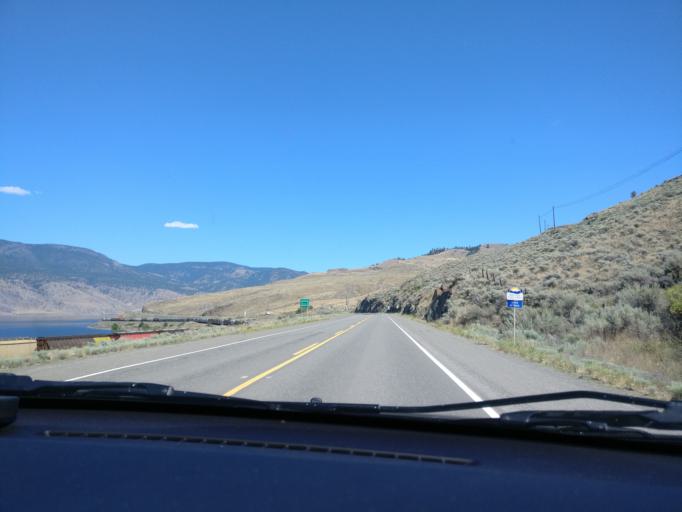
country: CA
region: British Columbia
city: Logan Lake
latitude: 50.7597
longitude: -120.8038
